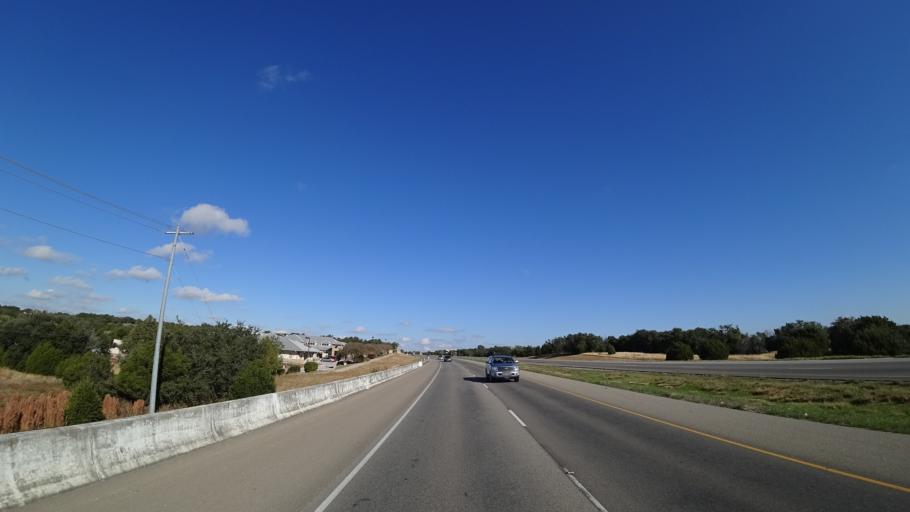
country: US
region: Texas
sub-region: Williamson County
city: Brushy Creek
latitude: 30.5149
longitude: -97.7737
